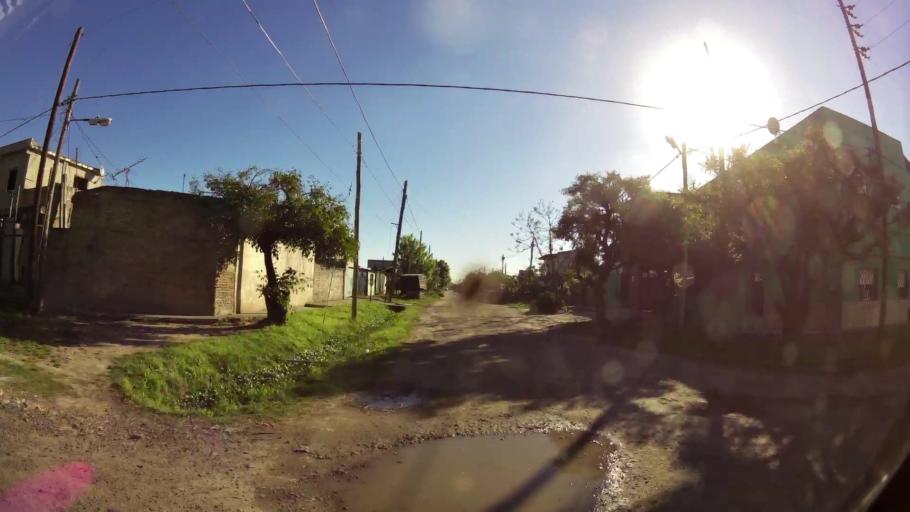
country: AR
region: Buenos Aires
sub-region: Partido de Quilmes
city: Quilmes
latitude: -34.7432
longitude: -58.3193
